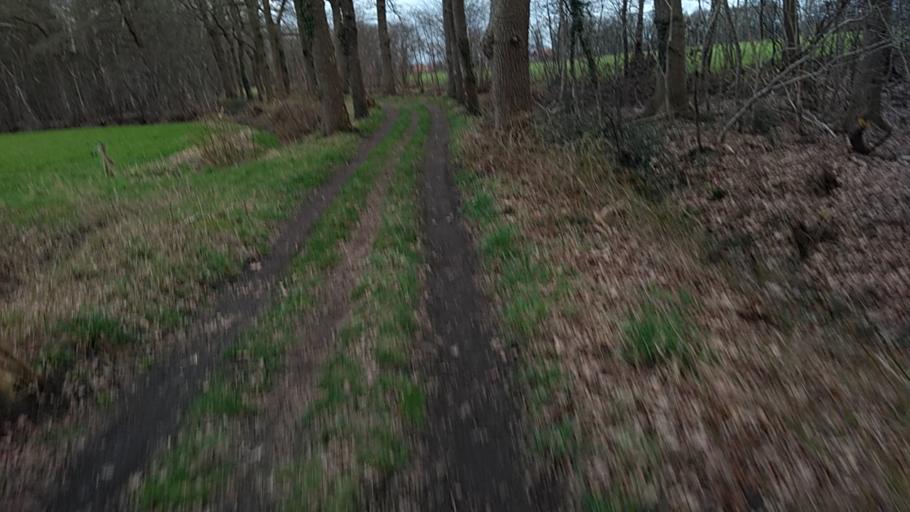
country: NL
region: Overijssel
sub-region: Gemeente Almelo
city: Almelo
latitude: 52.3587
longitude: 6.7103
